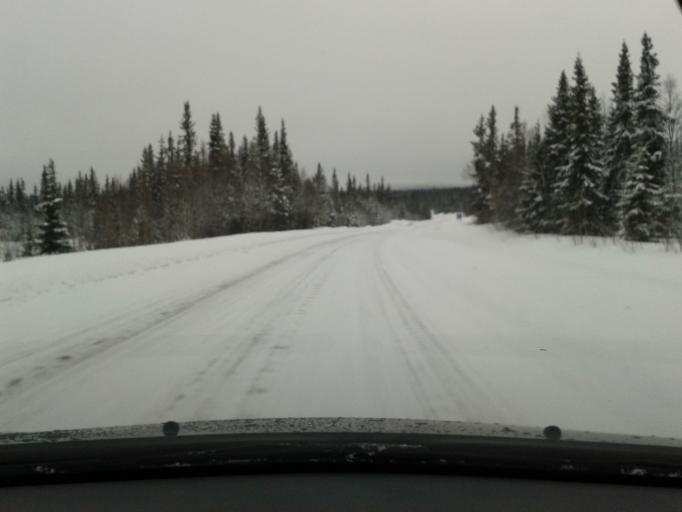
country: SE
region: Vaesterbotten
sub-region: Vilhelmina Kommun
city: Sjoberg
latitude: 65.1343
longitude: 15.8774
